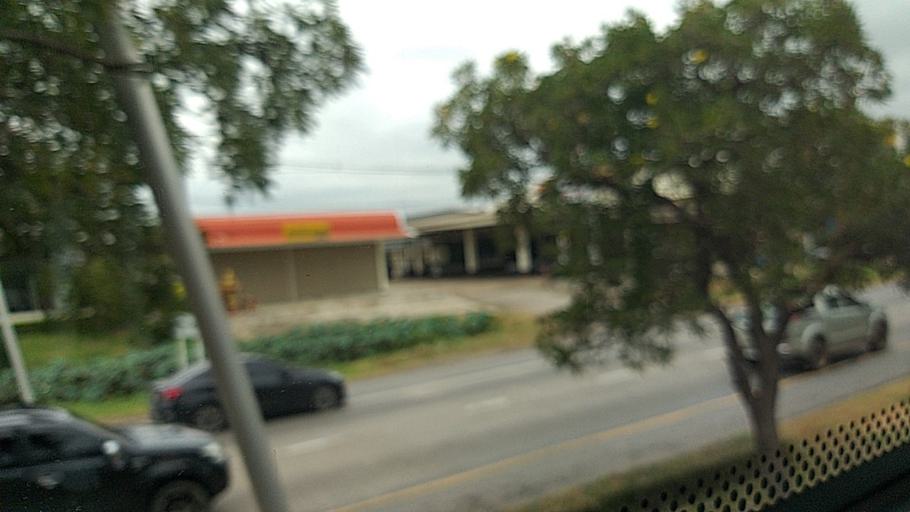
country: TH
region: Khon Kaen
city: Phon
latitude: 15.8104
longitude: 102.6075
